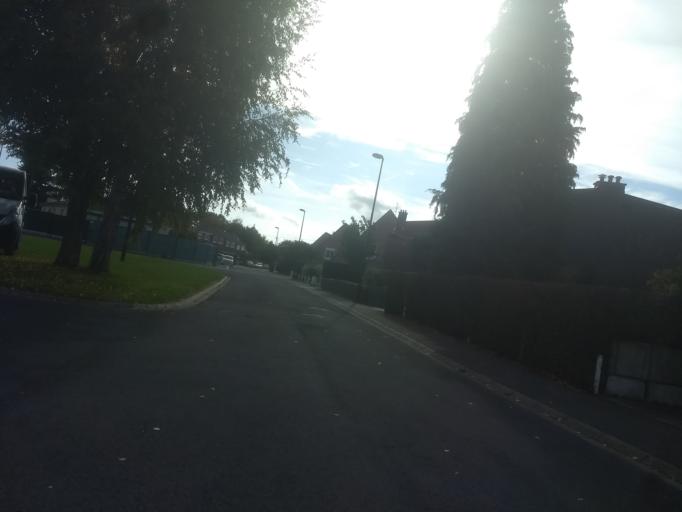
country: FR
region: Nord-Pas-de-Calais
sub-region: Departement du Pas-de-Calais
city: Dainville
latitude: 50.2855
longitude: 2.7313
